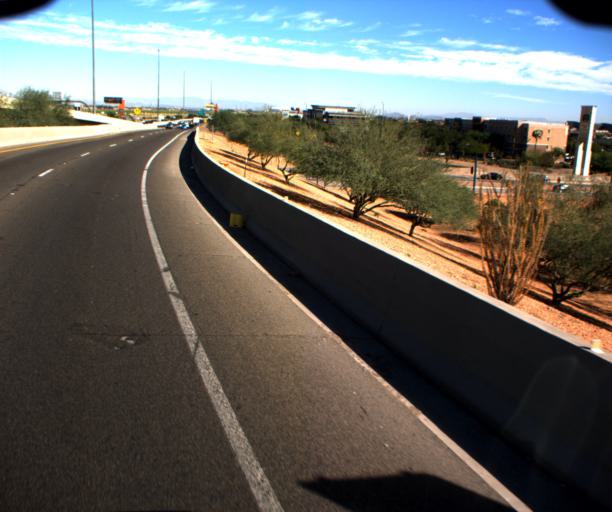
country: US
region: Arizona
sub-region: Maricopa County
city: Tolleson
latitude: 33.4638
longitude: -112.2682
